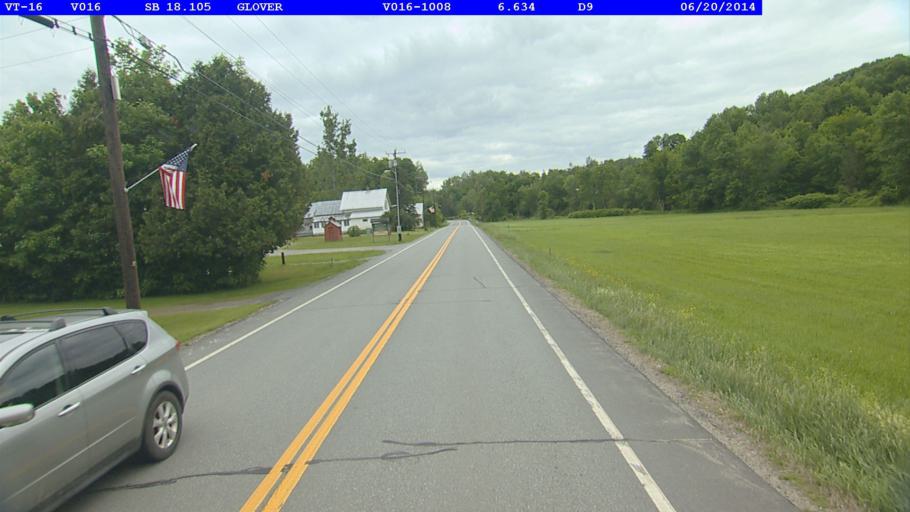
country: US
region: Vermont
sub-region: Orleans County
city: Newport
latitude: 44.7163
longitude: -72.1852
